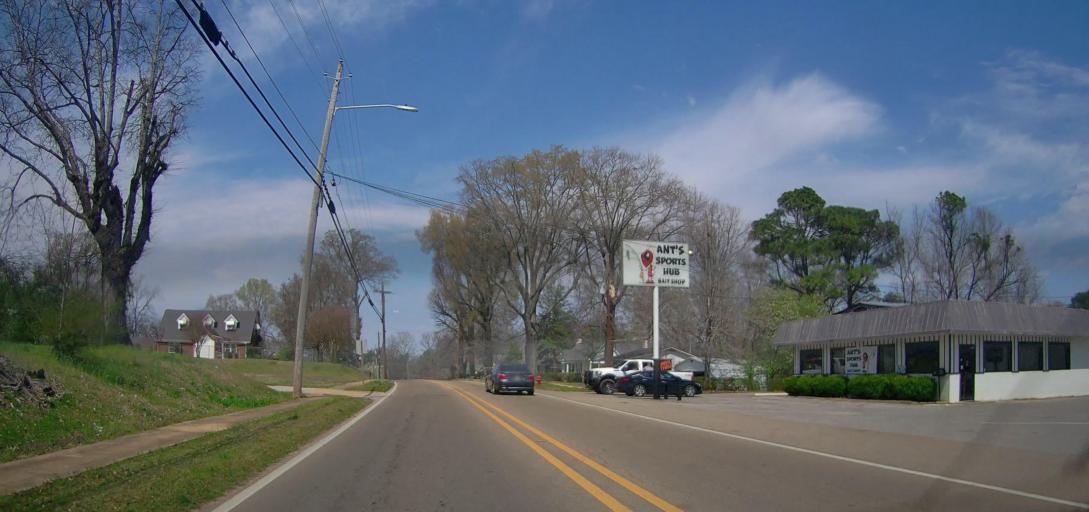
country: US
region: Mississippi
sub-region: Union County
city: New Albany
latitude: 34.4882
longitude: -89.0027
